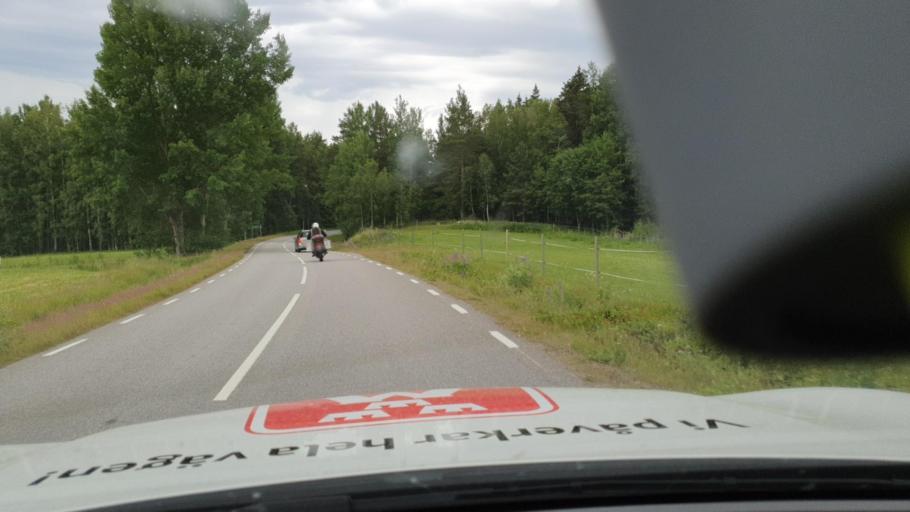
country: SE
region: Vaestra Goetaland
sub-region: Karlsborgs Kommun
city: Karlsborg
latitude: 58.7286
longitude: 14.5032
